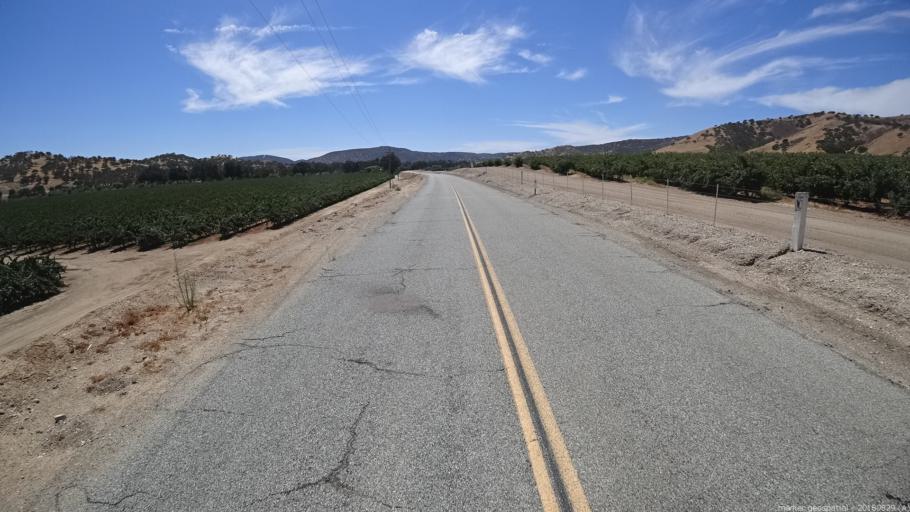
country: US
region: California
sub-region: San Luis Obispo County
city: Lake Nacimiento
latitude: 35.8132
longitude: -120.8468
